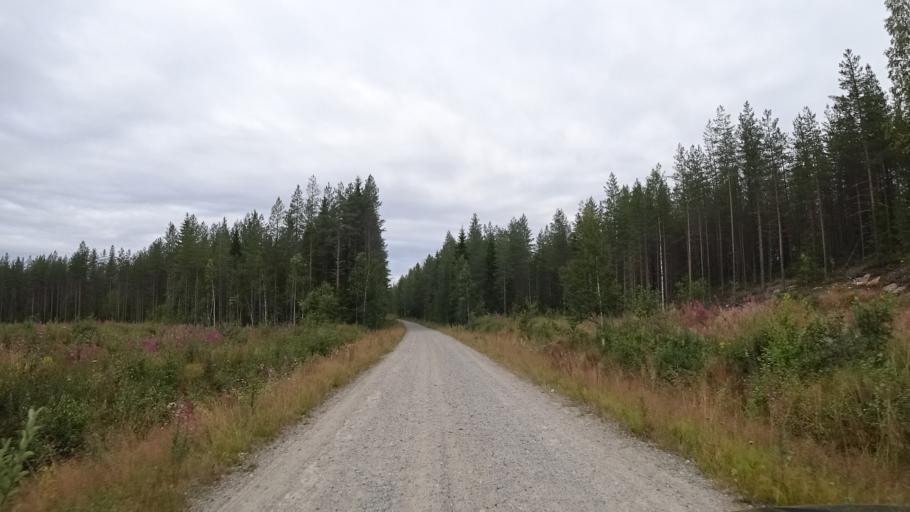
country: FI
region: North Karelia
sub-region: Joensuu
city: Ilomantsi
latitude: 63.1533
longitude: 30.6422
